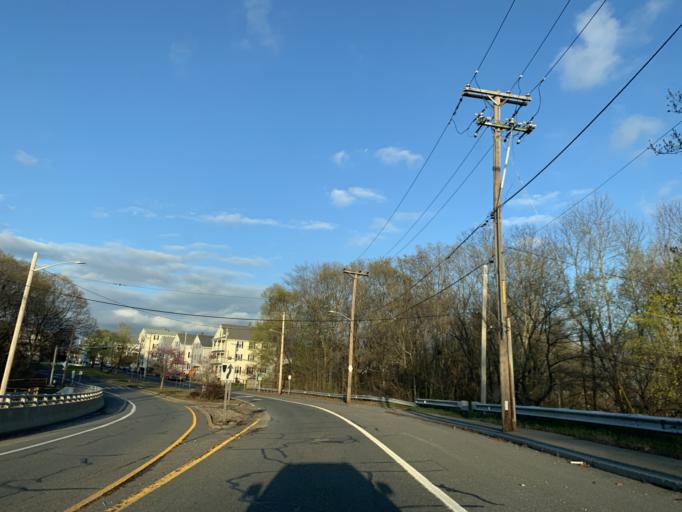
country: US
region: Rhode Island
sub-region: Providence County
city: Valley Falls
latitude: 41.9062
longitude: -71.3989
